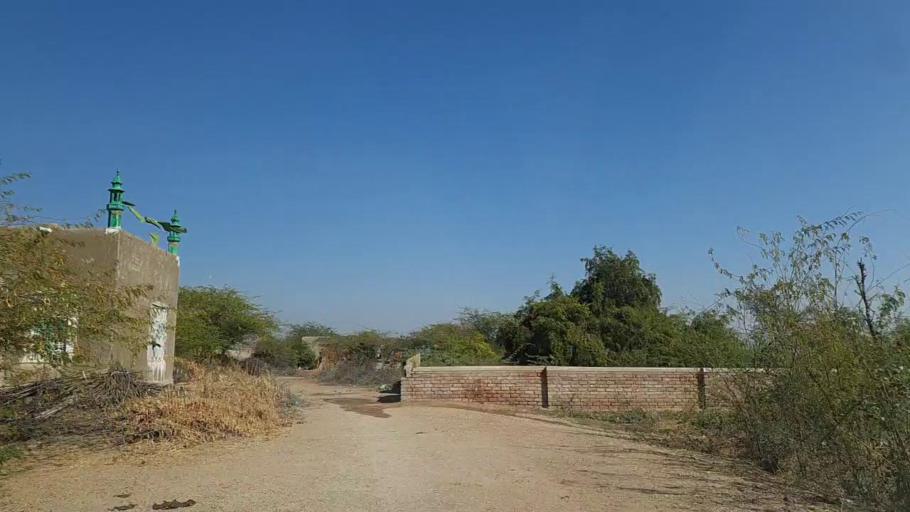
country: PK
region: Sindh
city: Samaro
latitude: 25.3965
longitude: 69.4320
